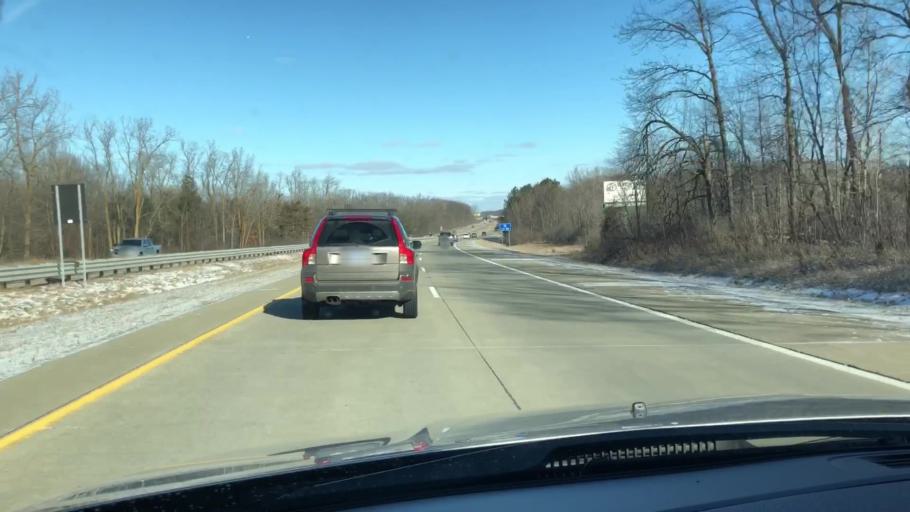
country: US
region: Michigan
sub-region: Genesee County
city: Lake Fenton
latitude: 42.8481
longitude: -83.7393
